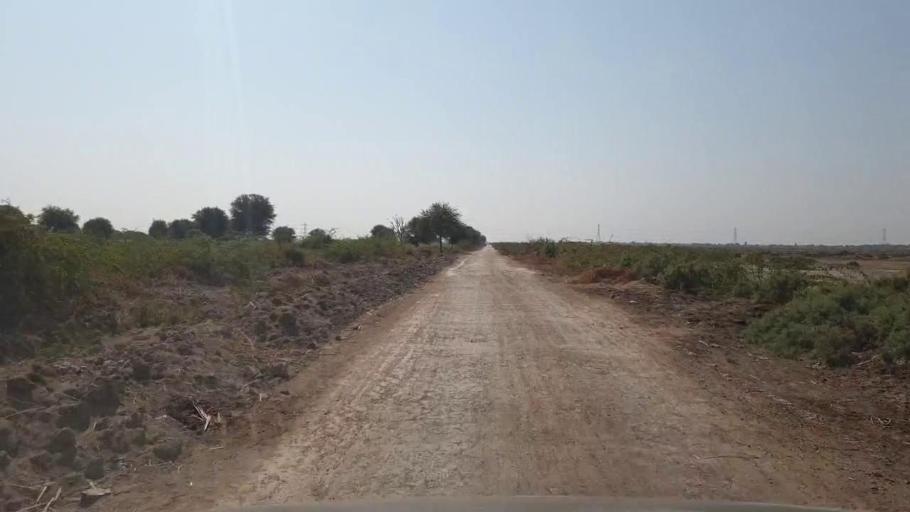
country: PK
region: Sindh
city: Digri
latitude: 25.1998
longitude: 69.2275
